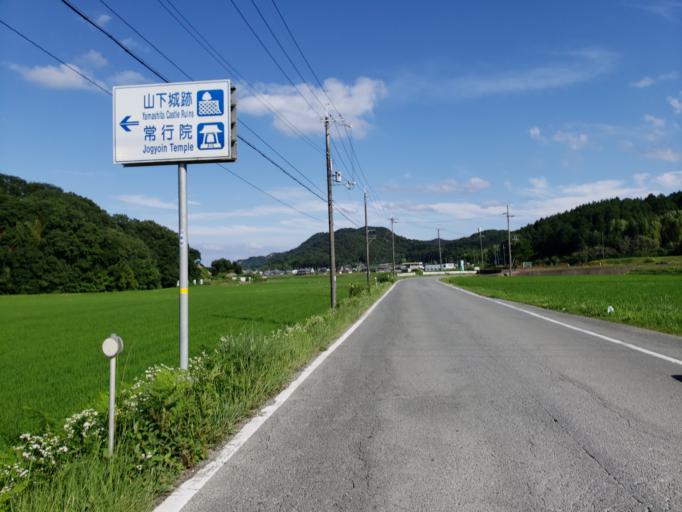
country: JP
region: Hyogo
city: Himeji
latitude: 34.9015
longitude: 134.7967
